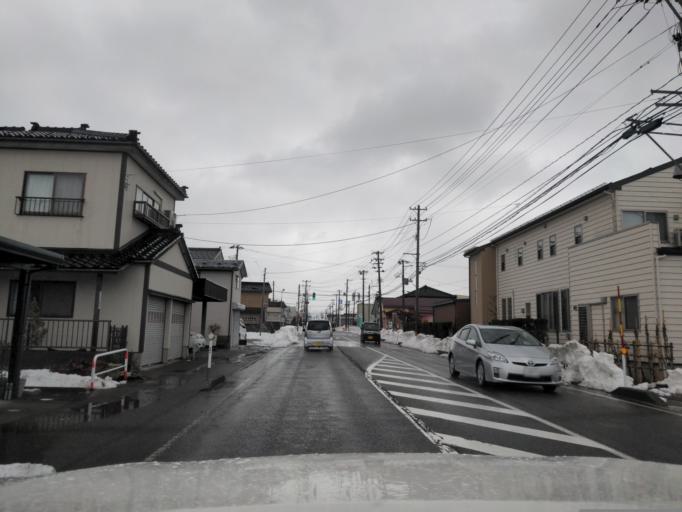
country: JP
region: Niigata
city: Kashiwazaki
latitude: 37.3587
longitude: 138.5661
